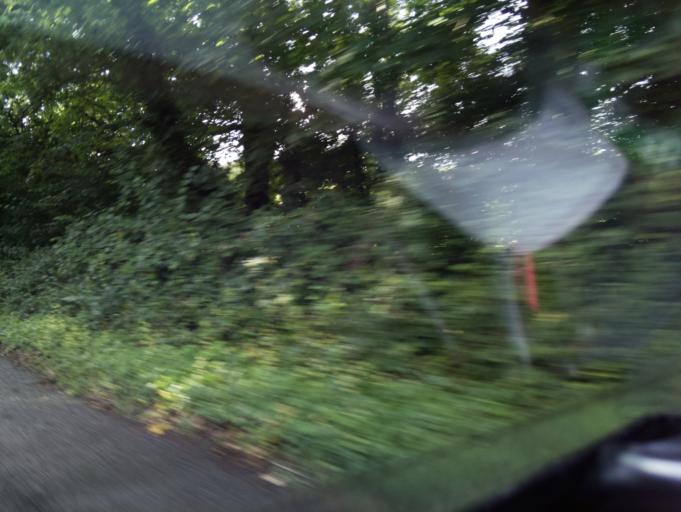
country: GB
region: England
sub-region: Devon
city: South Brent
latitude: 50.4004
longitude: -3.8020
